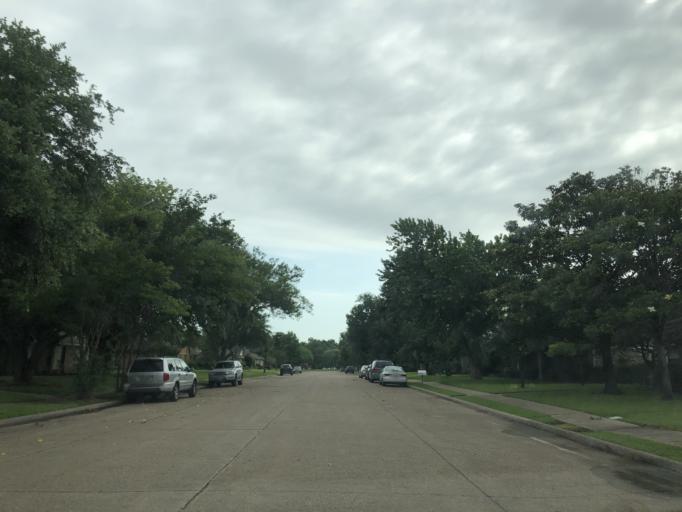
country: US
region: Texas
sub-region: Dallas County
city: Sunnyvale
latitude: 32.8430
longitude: -96.6139
